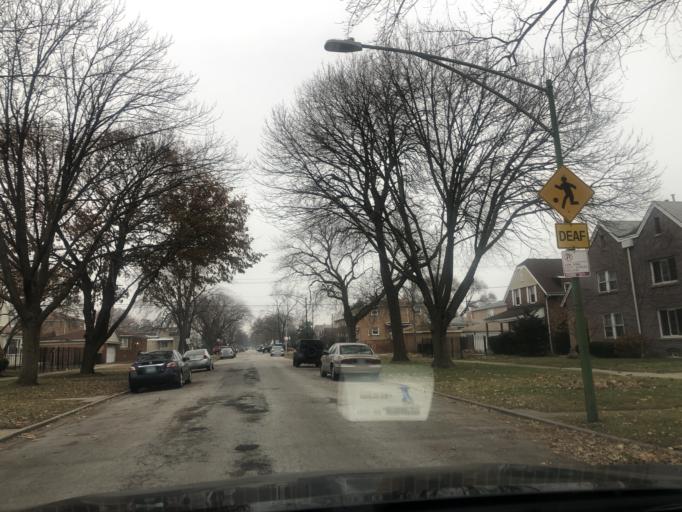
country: US
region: Illinois
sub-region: Cook County
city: Evergreen Park
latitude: 41.7353
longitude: -87.6210
